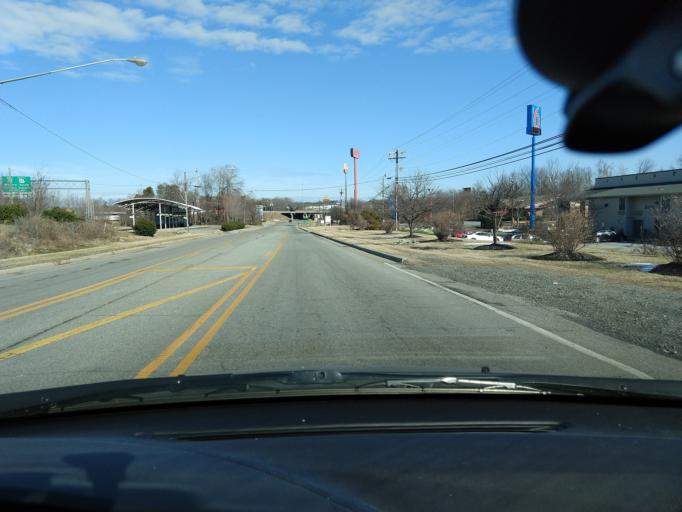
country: US
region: North Carolina
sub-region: Guilford County
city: Jamestown
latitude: 36.0763
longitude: -79.9582
